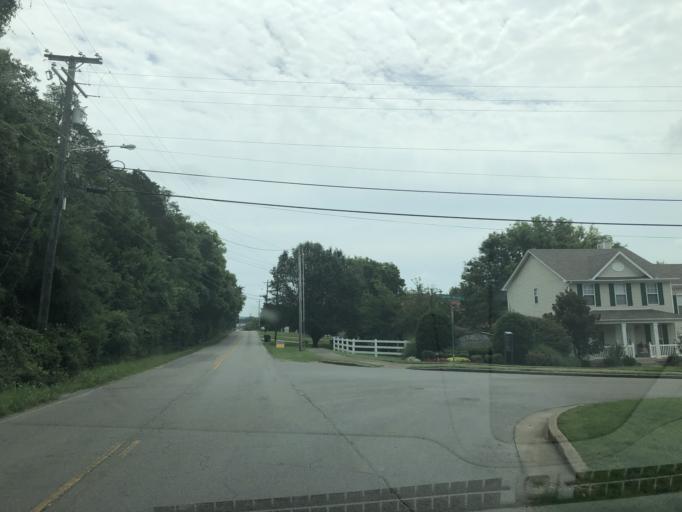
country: US
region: Tennessee
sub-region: Williamson County
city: Nolensville
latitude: 36.0232
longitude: -86.6863
